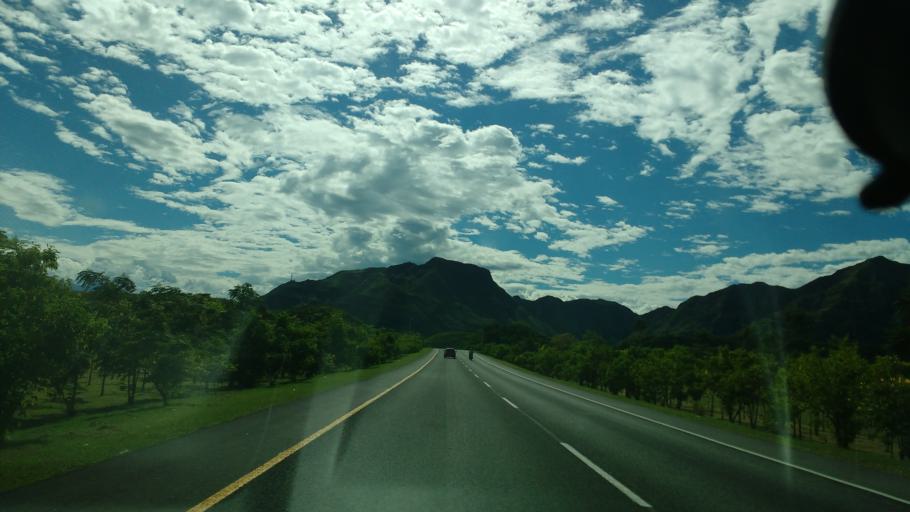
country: CO
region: Tolima
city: Valle de San Juan
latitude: 4.2739
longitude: -75.0024
